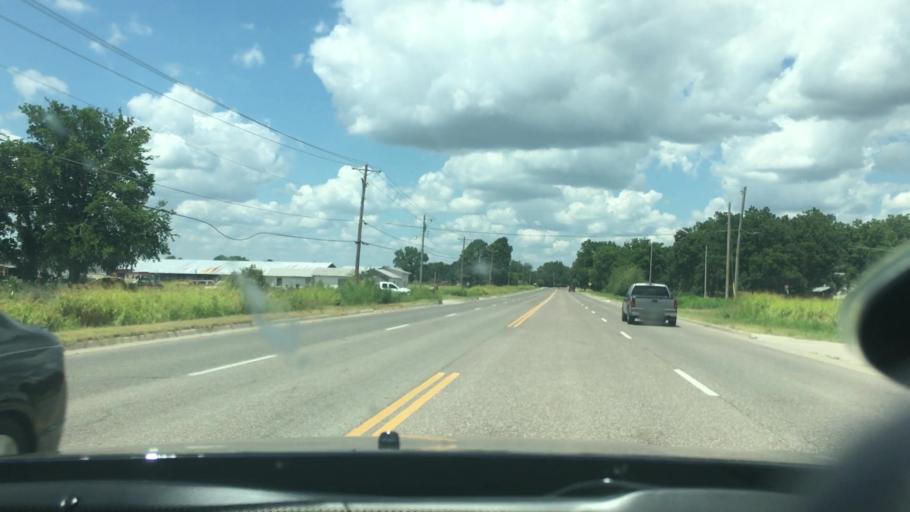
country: US
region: Oklahoma
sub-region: Murray County
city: Davis
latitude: 34.4694
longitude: -97.1314
